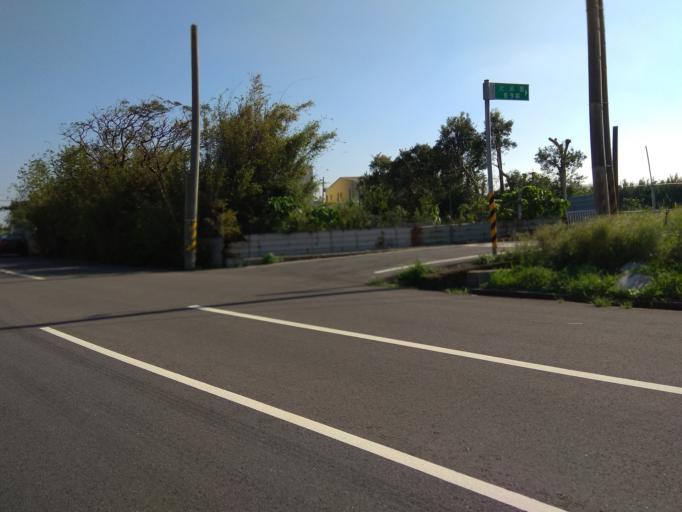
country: TW
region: Taiwan
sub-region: Hsinchu
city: Zhubei
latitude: 25.0322
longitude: 121.0744
